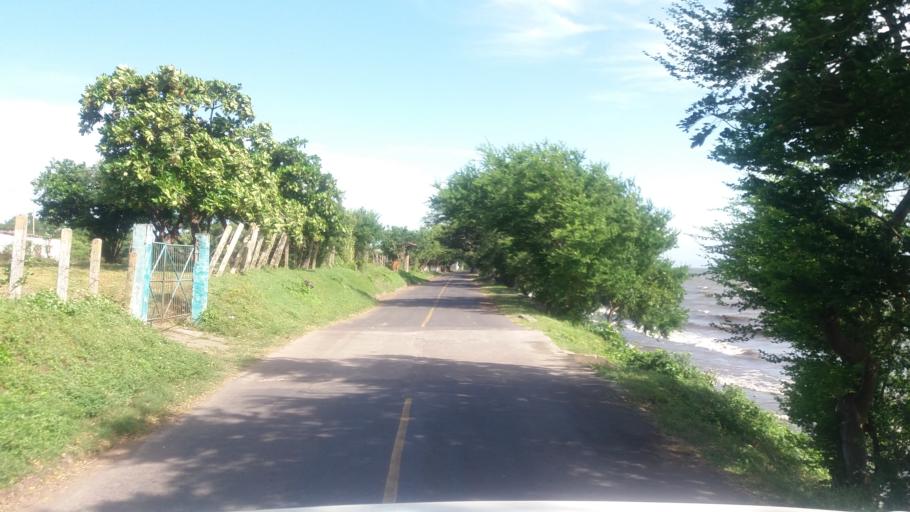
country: NI
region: Granada
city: Granada
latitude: 11.9529
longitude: -85.9457
